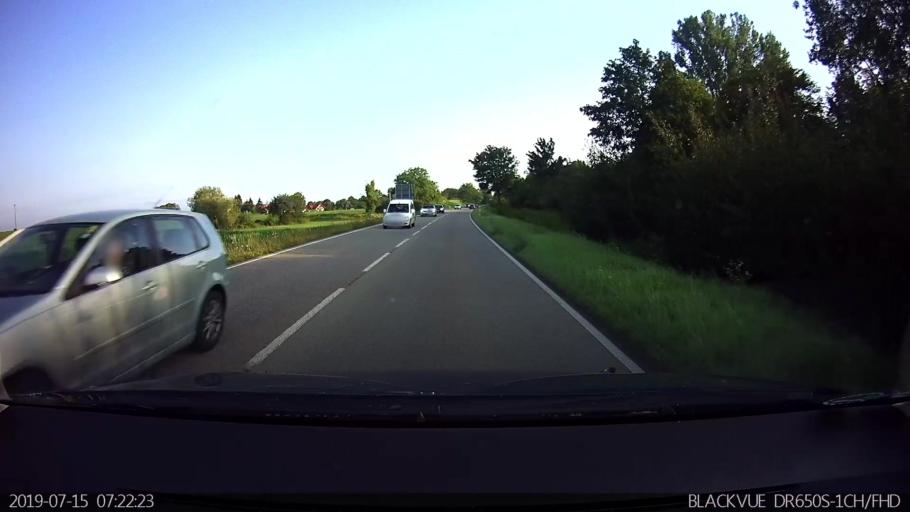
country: DE
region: Baden-Wuerttemberg
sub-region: Freiburg Region
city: Unterkrozingen
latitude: 47.9298
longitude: 7.6892
